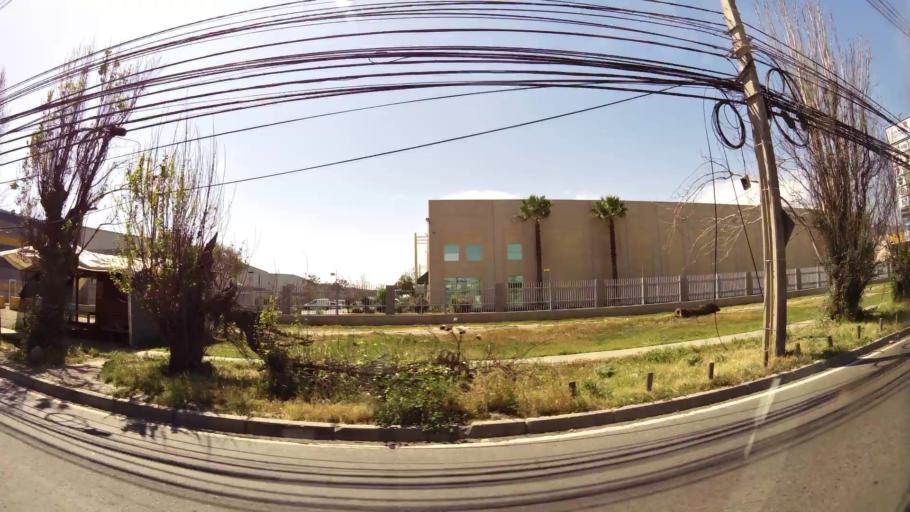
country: CL
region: Santiago Metropolitan
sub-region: Provincia de Santiago
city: Lo Prado
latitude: -33.3845
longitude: -70.7635
